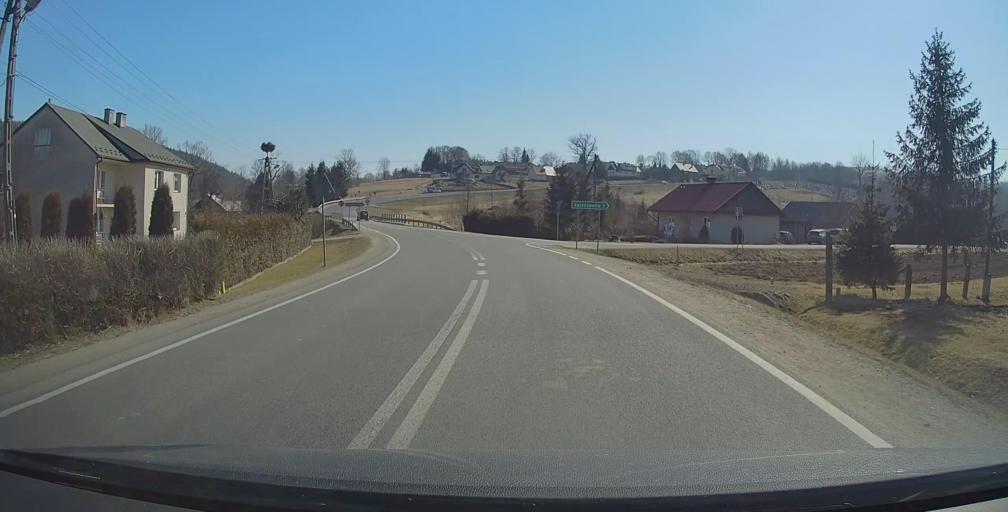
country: PL
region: Subcarpathian Voivodeship
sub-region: Powiat przemyski
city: Bircza
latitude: 49.6635
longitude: 22.4328
